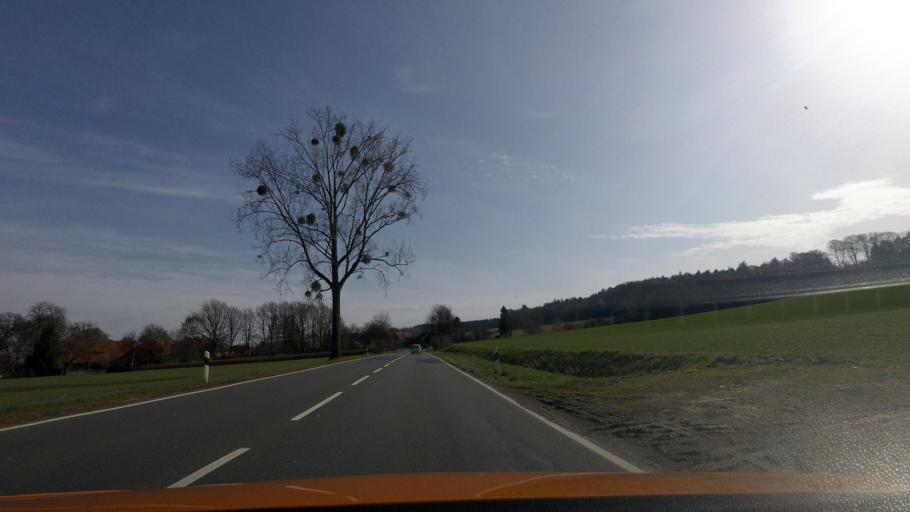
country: DE
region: Lower Saxony
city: Heuerssen
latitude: 52.3370
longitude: 9.2931
